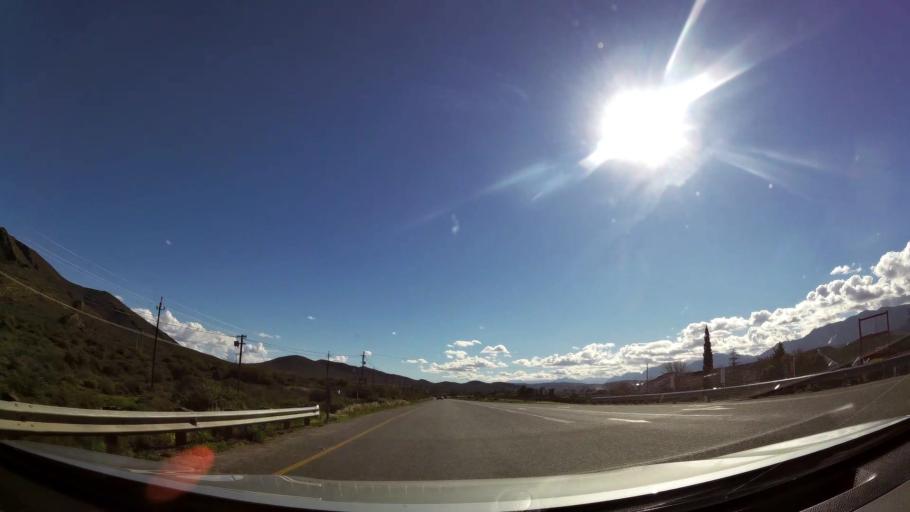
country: ZA
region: Western Cape
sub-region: Cape Winelands District Municipality
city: Ashton
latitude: -33.7775
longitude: 19.7620
